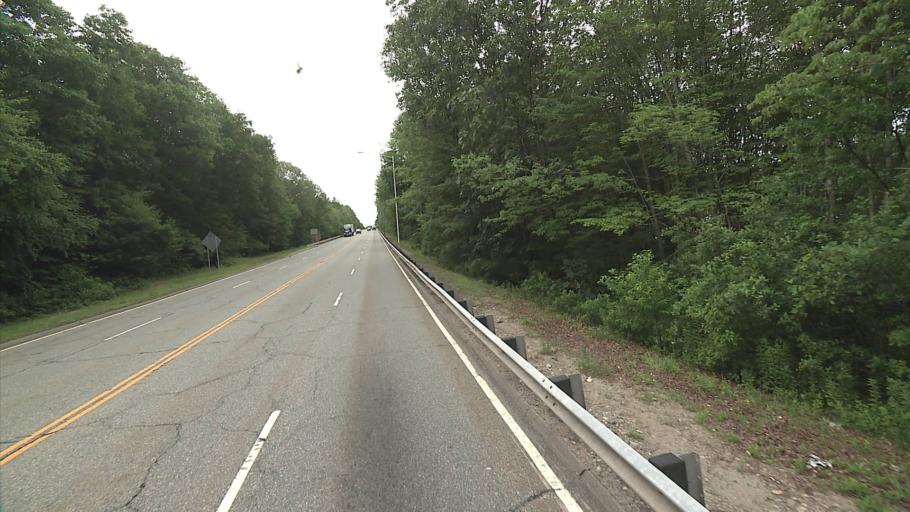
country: US
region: Connecticut
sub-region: New London County
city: Groton
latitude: 41.3530
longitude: -72.0697
